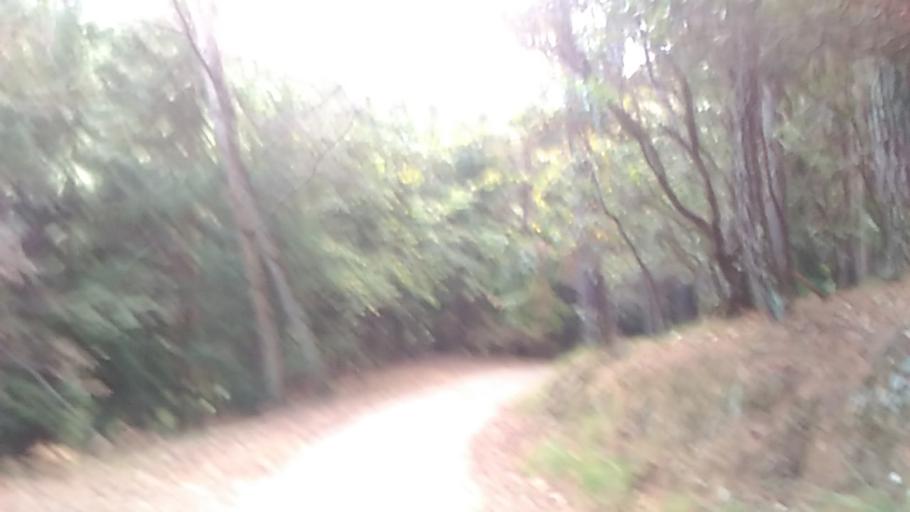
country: TW
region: Taiwan
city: Daxi
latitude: 24.4049
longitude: 121.3055
